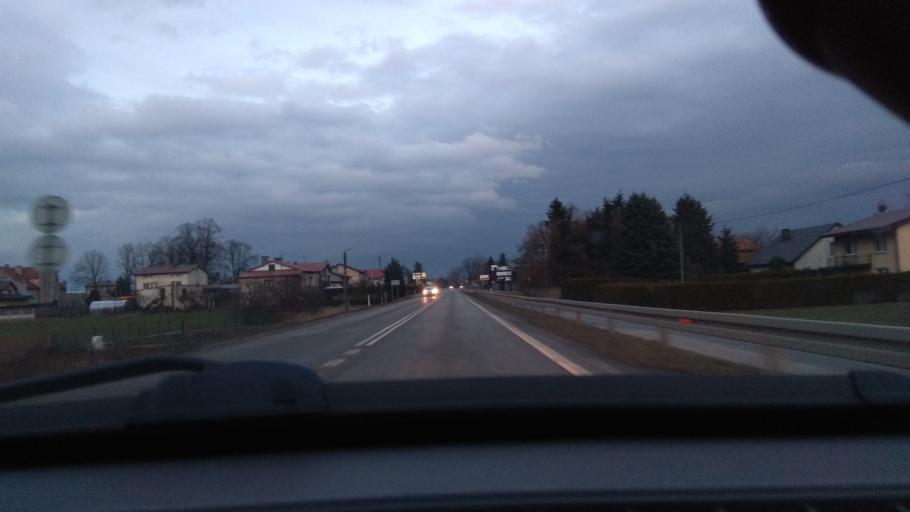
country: PL
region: Greater Poland Voivodeship
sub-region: Powiat kepinski
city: Baranow
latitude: 51.2924
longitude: 18.0297
